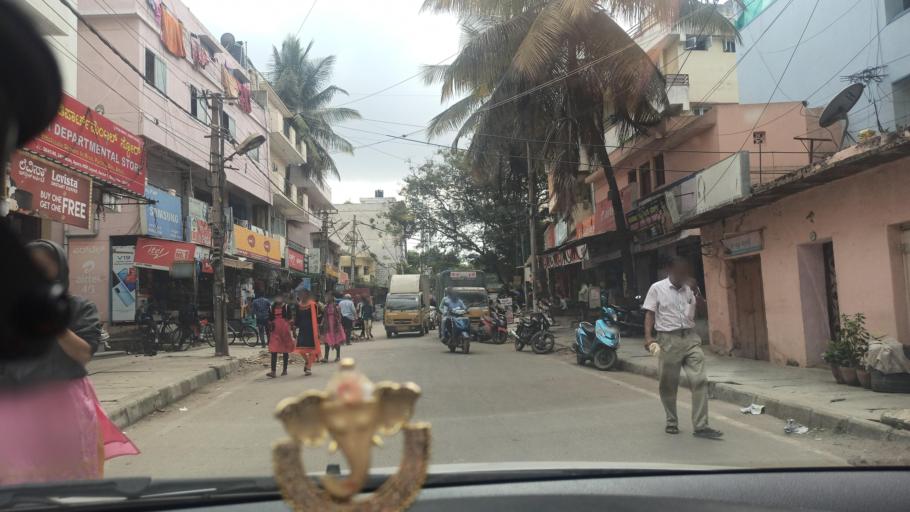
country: IN
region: Karnataka
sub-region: Bangalore Urban
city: Bangalore
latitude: 12.9222
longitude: 77.6497
